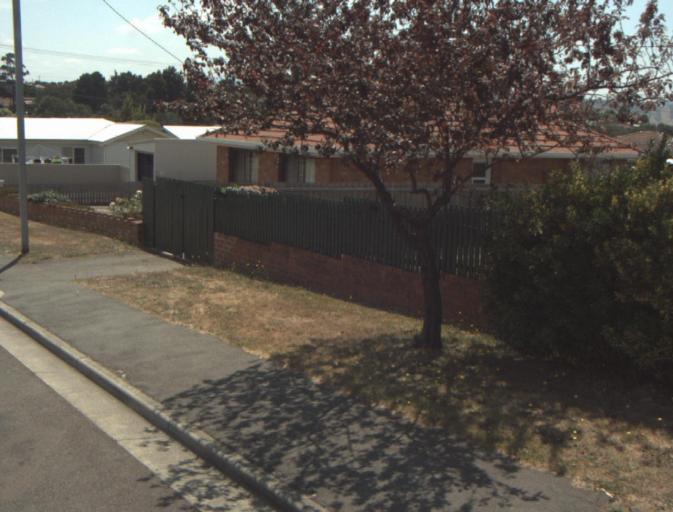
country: AU
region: Tasmania
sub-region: Launceston
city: Summerhill
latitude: -41.4858
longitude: 147.1697
